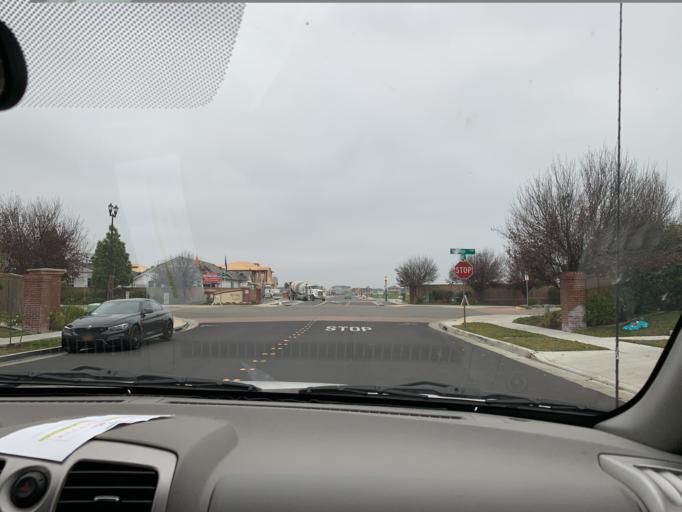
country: US
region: California
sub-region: Yolo County
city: Woodland
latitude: 38.6476
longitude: -121.7403
